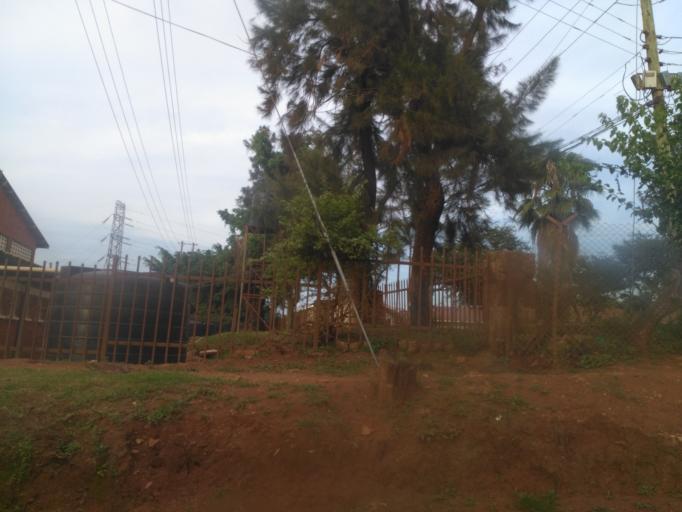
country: UG
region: Central Region
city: Kampala Central Division
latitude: 0.3456
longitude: 32.5750
